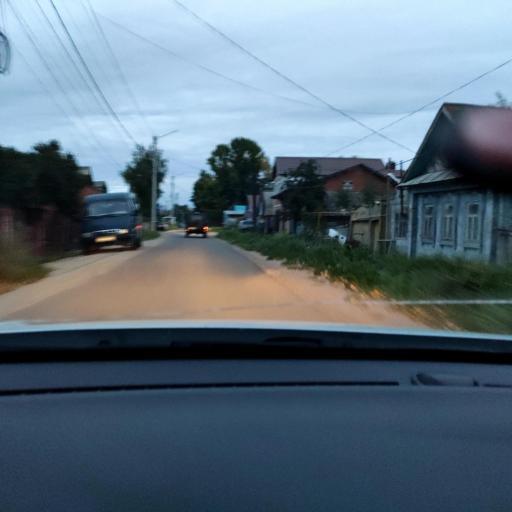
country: RU
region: Mariy-El
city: Volzhsk
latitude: 55.8685
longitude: 48.3636
